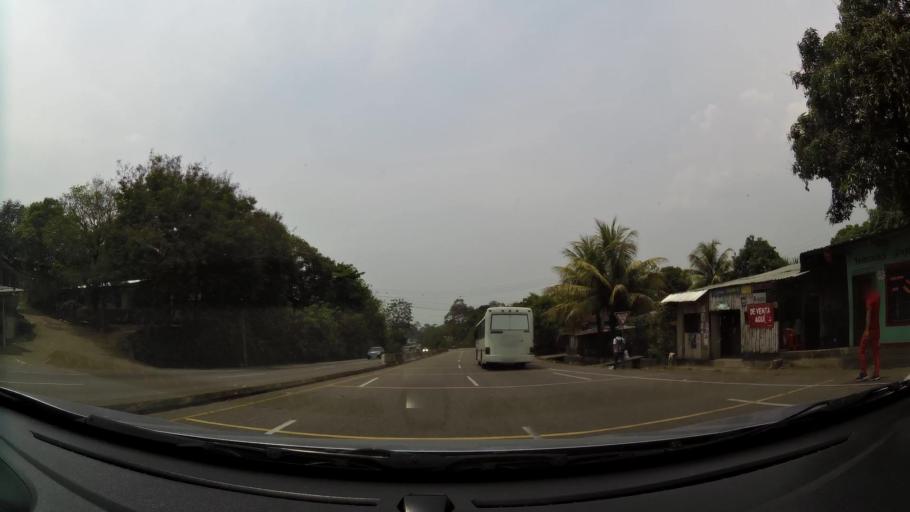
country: HN
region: Cortes
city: Oropendolas
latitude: 14.9882
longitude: -87.9297
